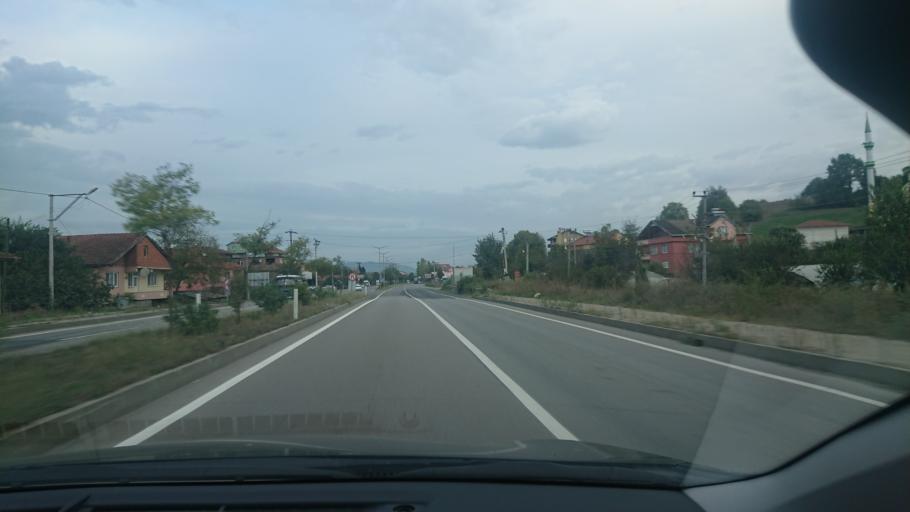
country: TR
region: Zonguldak
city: Gokcebey
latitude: 41.3297
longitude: 32.0946
